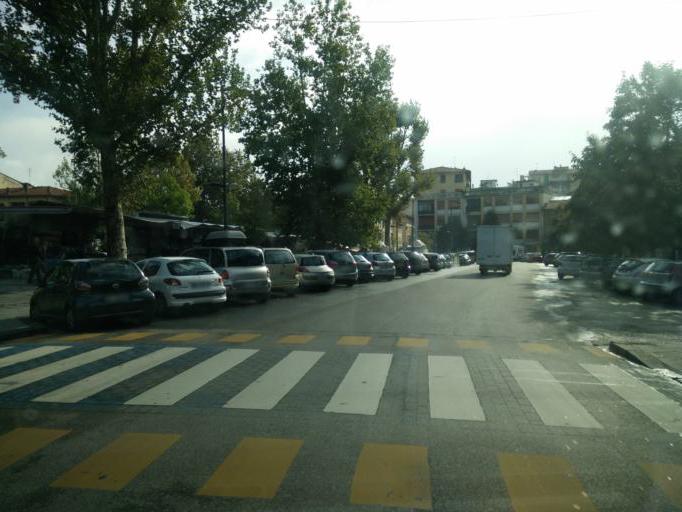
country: IT
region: Tuscany
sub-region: Province of Florence
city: Florence
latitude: 43.7860
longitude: 11.2275
